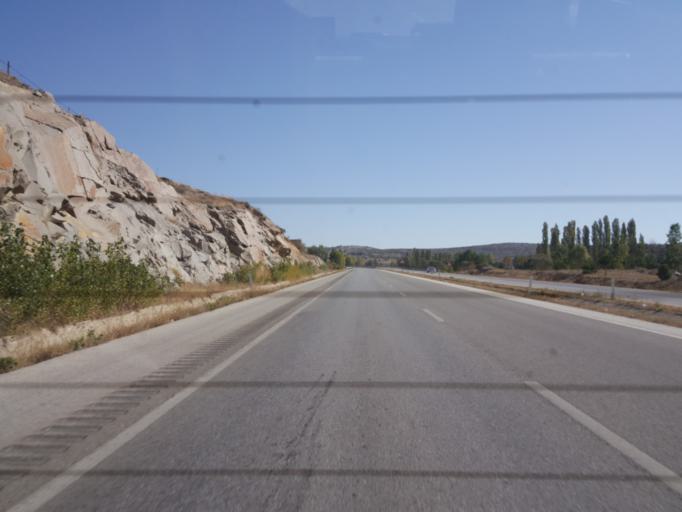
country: TR
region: Corum
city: Alaca
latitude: 40.2622
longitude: 34.6297
